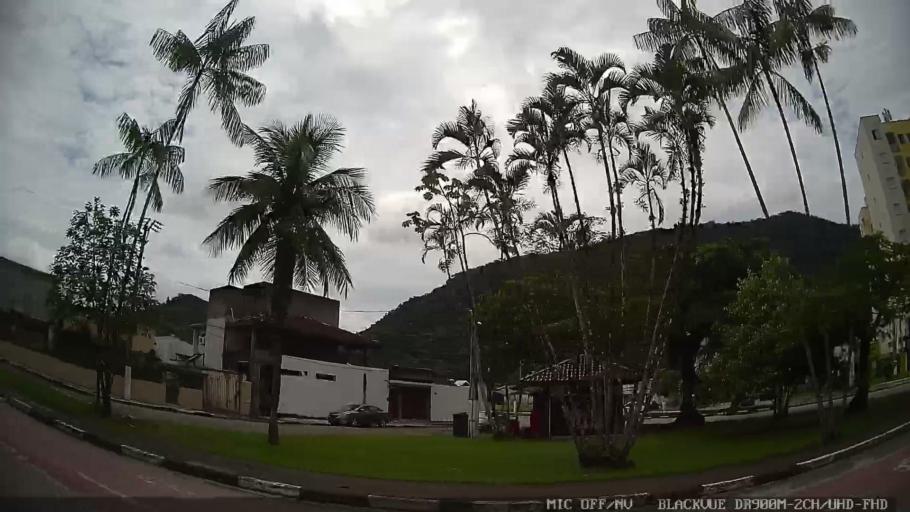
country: BR
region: Sao Paulo
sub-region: Caraguatatuba
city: Caraguatatuba
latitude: -23.6194
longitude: -45.4039
